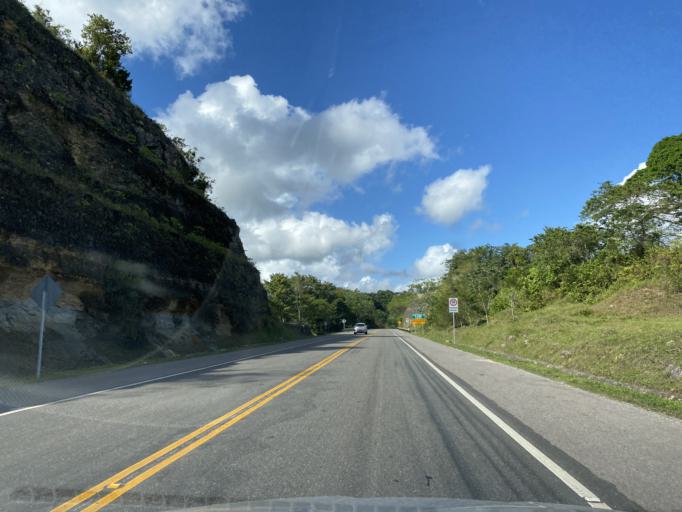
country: DO
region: Monte Plata
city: Majagual
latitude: 19.0440
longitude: -69.8308
